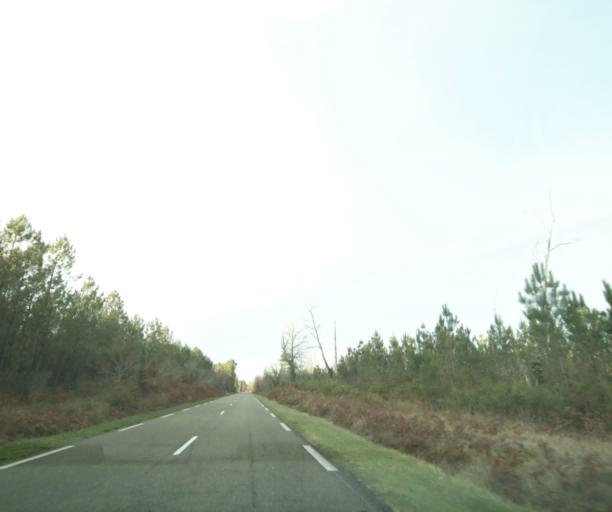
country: FR
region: Aquitaine
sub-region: Departement des Landes
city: Gabarret
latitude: 44.0485
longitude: -0.0409
